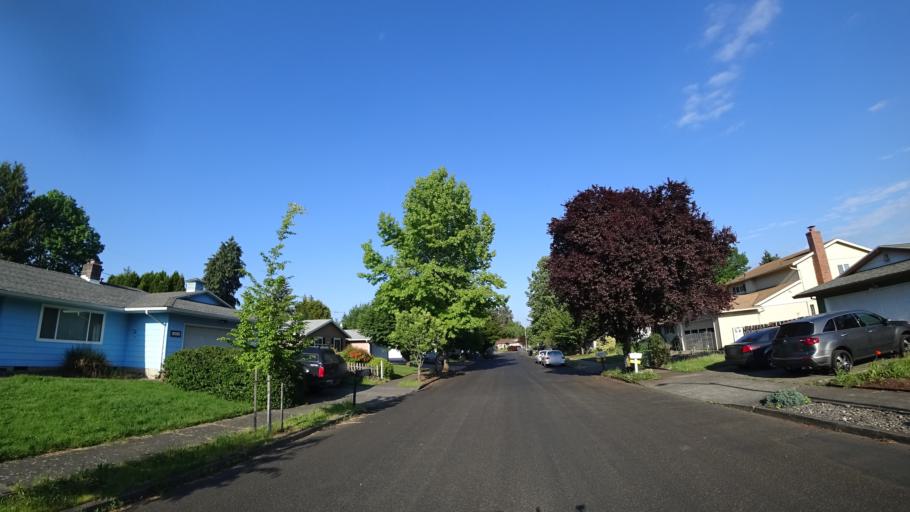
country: US
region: Oregon
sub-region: Multnomah County
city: Gresham
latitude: 45.5097
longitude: -122.4948
